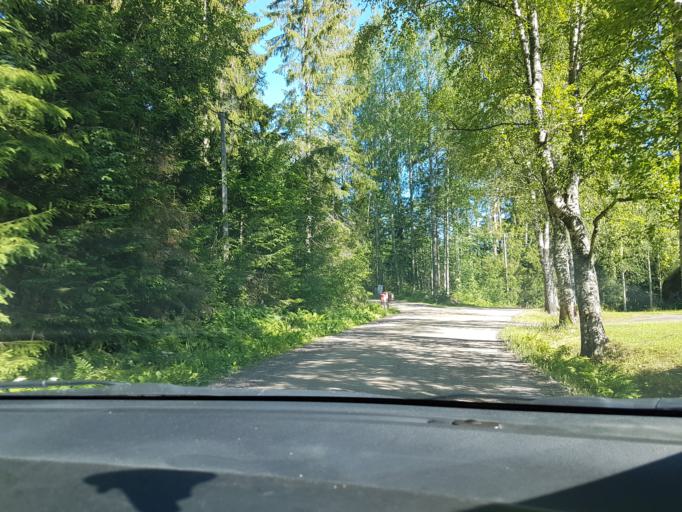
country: FI
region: Uusimaa
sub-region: Helsinki
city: Sibbo
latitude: 60.2870
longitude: 25.2398
